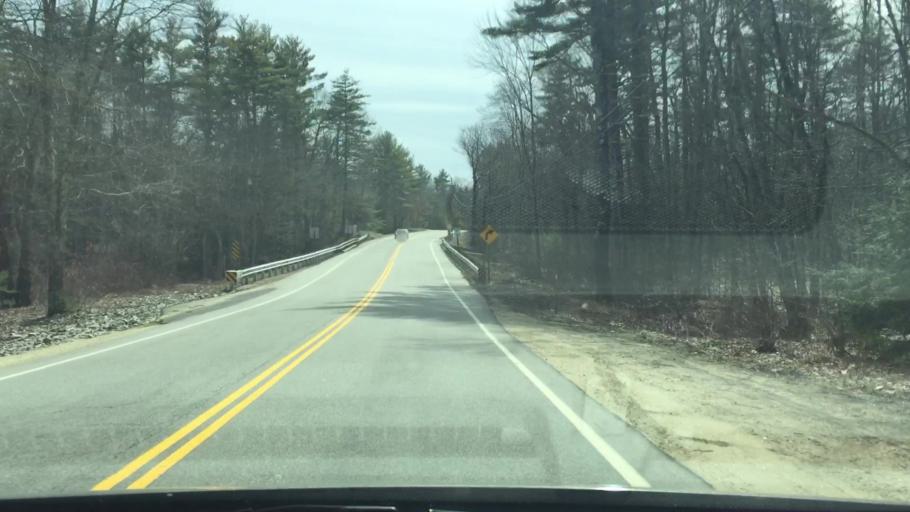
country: US
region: New Hampshire
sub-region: Strafford County
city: Barrington
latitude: 43.2409
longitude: -71.0550
